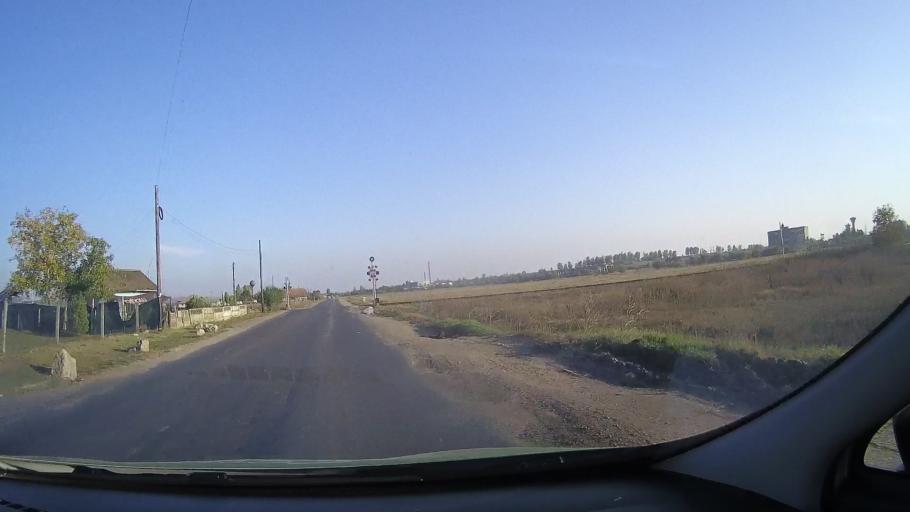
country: RO
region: Bihor
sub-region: Comuna Bors
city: Santion
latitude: 47.1079
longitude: 21.8681
